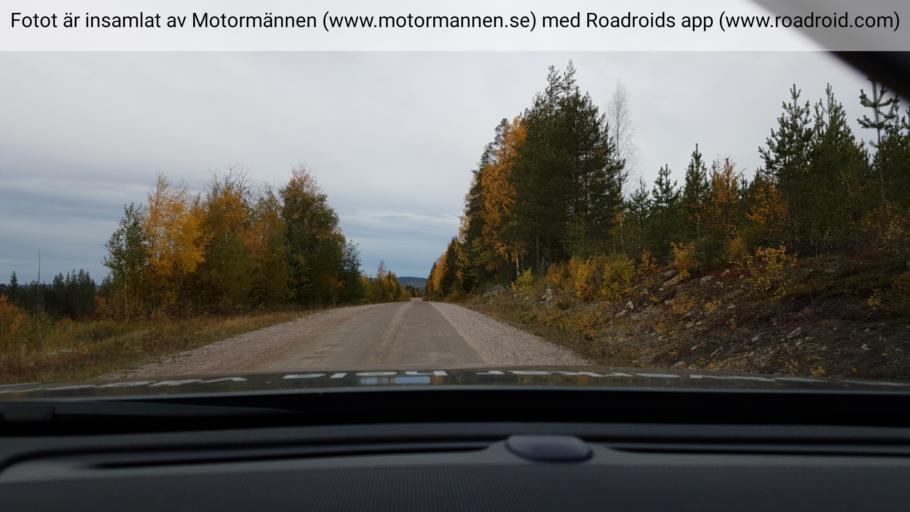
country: SE
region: Norrbotten
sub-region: Overkalix Kommun
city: OEverkalix
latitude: 66.2629
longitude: 23.0217
